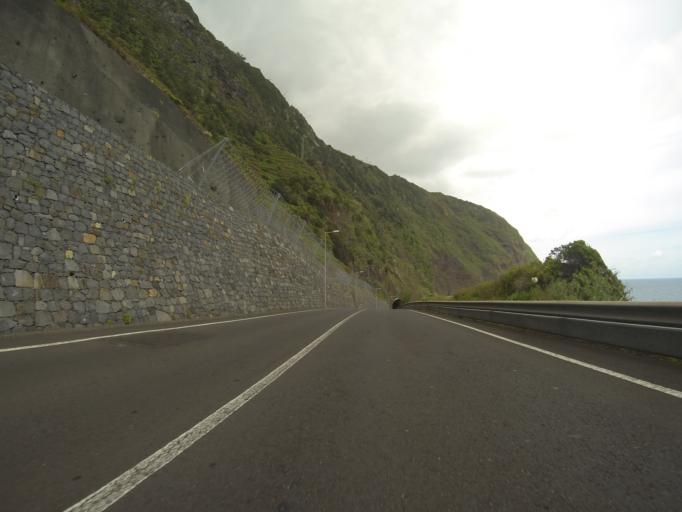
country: PT
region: Madeira
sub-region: Porto Moniz
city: Porto Moniz
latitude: 32.8475
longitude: -17.1492
